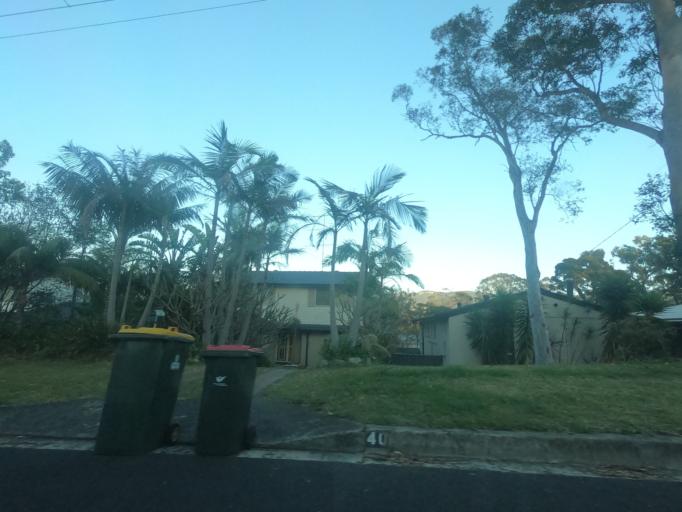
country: AU
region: New South Wales
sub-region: Wollongong
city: Dapto
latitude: -34.5111
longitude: 150.7824
